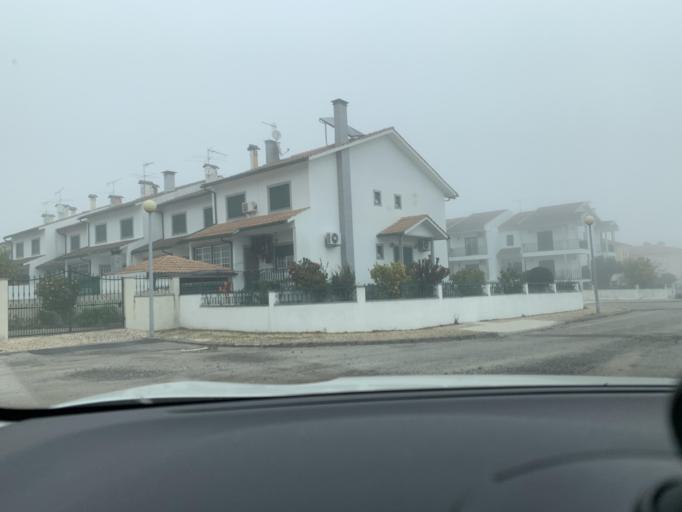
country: PT
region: Viseu
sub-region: Viseu
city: Rio de Loba
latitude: 40.6407
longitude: -7.8651
